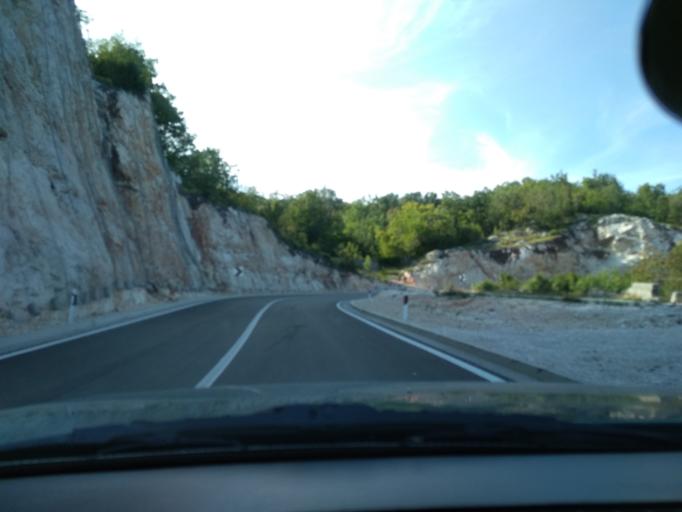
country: ME
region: Cetinje
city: Cetinje
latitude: 42.4085
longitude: 18.8875
